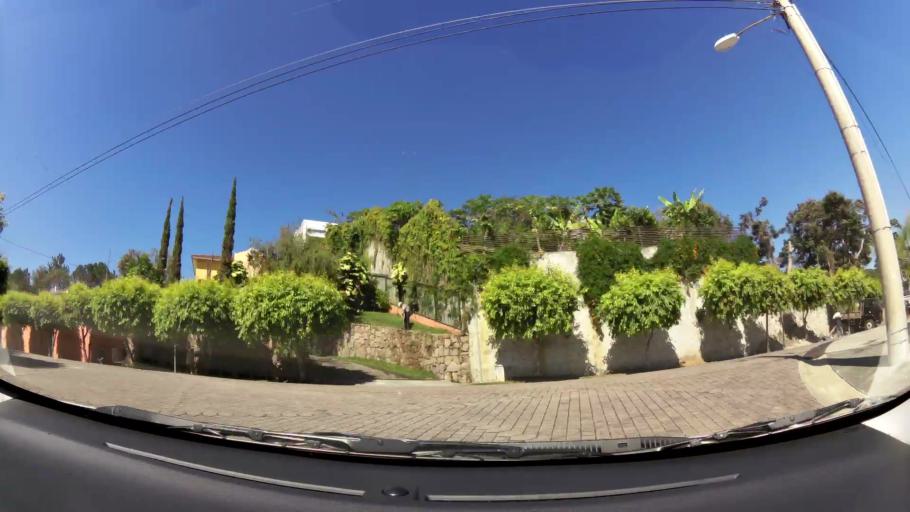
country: SV
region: La Libertad
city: Nuevo Cuscatlan
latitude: 13.6564
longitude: -89.2824
